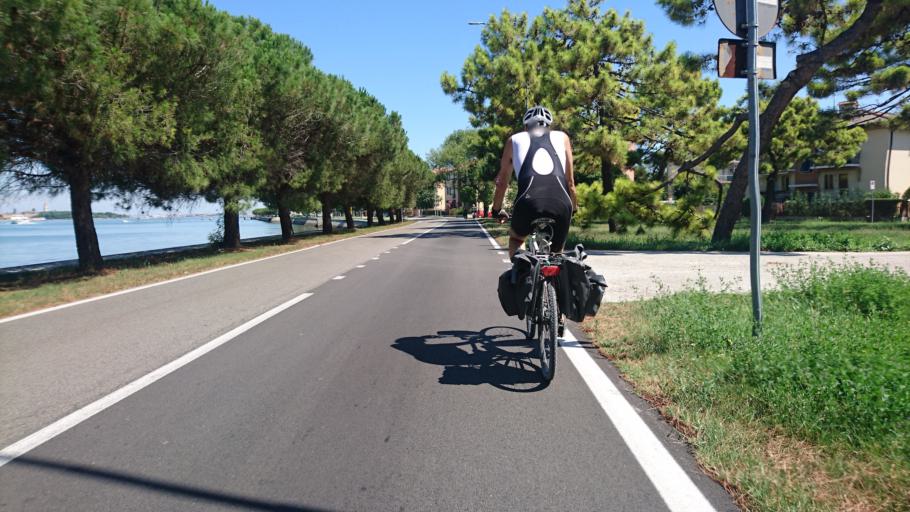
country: IT
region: Veneto
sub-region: Provincia di Venezia
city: Lido
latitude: 45.3686
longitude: 12.3365
